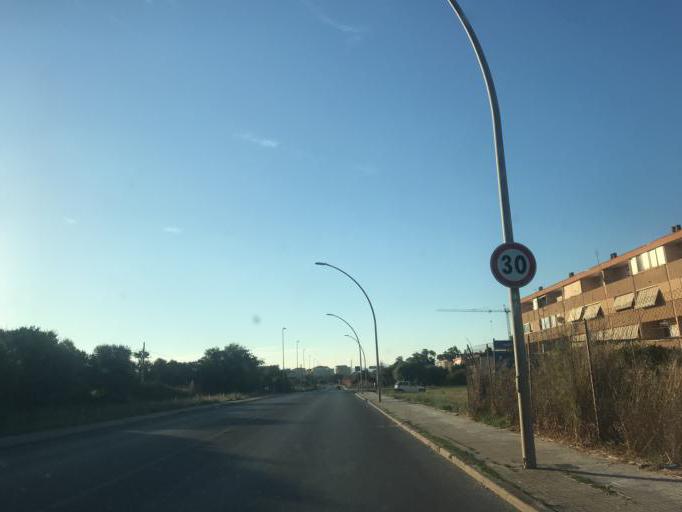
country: IT
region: Sardinia
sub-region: Provincia di Sassari
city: Alghero
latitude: 40.5668
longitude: 8.3303
